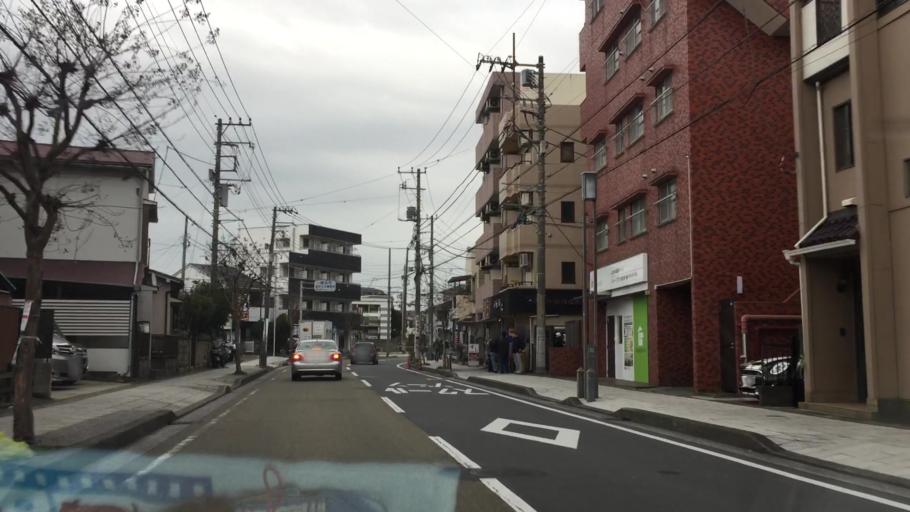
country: JP
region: Kanagawa
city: Zushi
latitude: 35.3399
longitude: 139.6262
